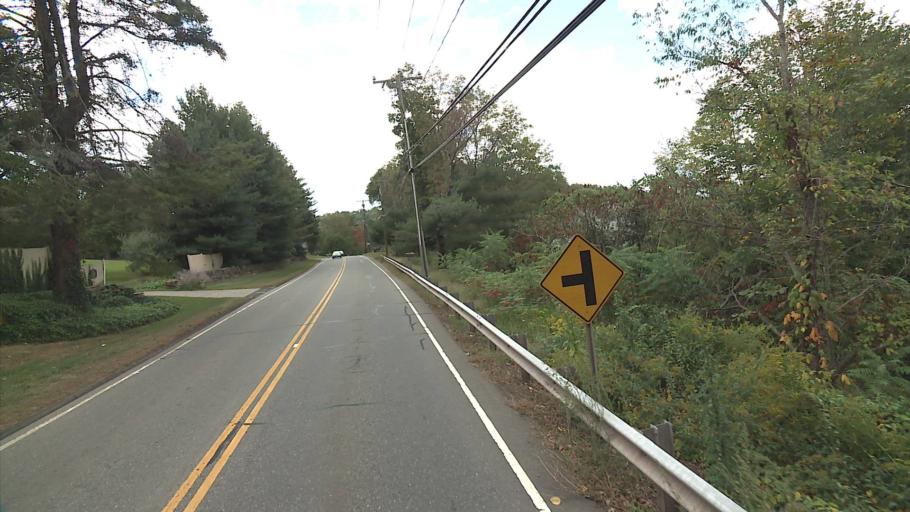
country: US
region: Connecticut
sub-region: Middlesex County
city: Durham
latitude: 41.5022
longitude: -72.7165
